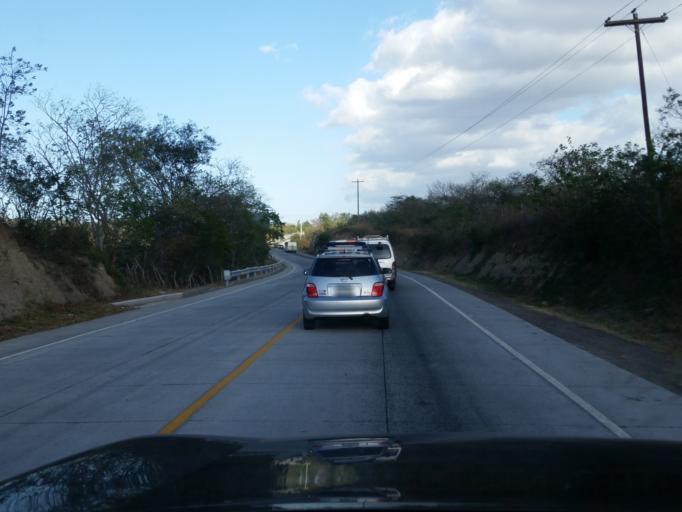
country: NI
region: Managua
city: Ciudad Sandino
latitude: 12.0817
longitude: -86.4114
